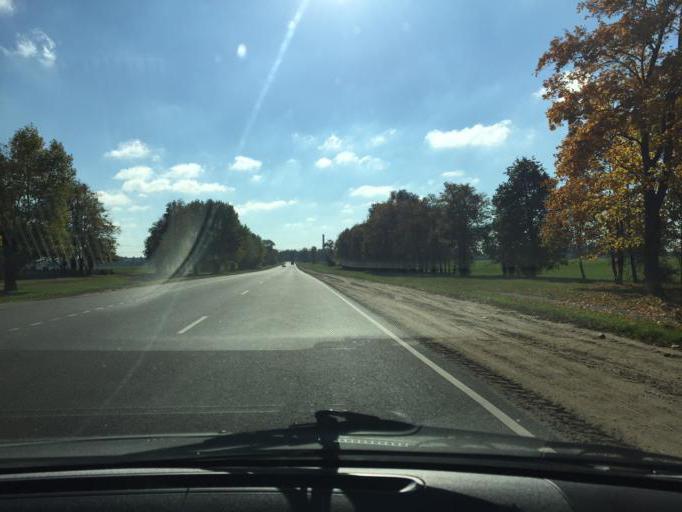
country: BY
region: Minsk
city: Slutsk
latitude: 53.0625
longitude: 27.5536
